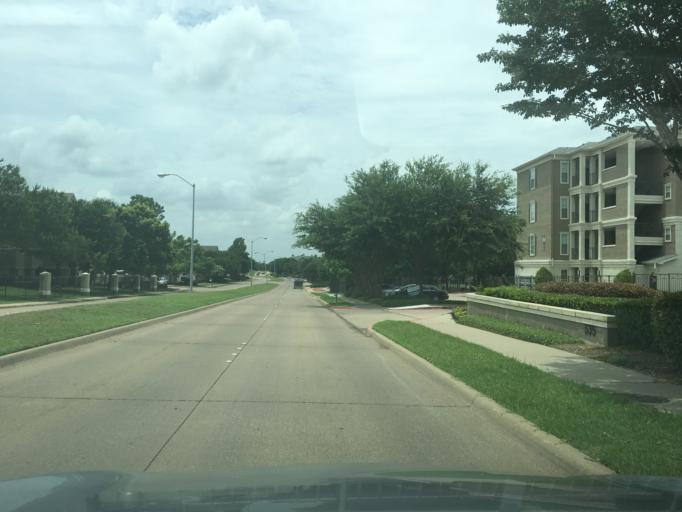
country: US
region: Texas
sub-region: Dallas County
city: Richardson
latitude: 32.9350
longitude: -96.7235
